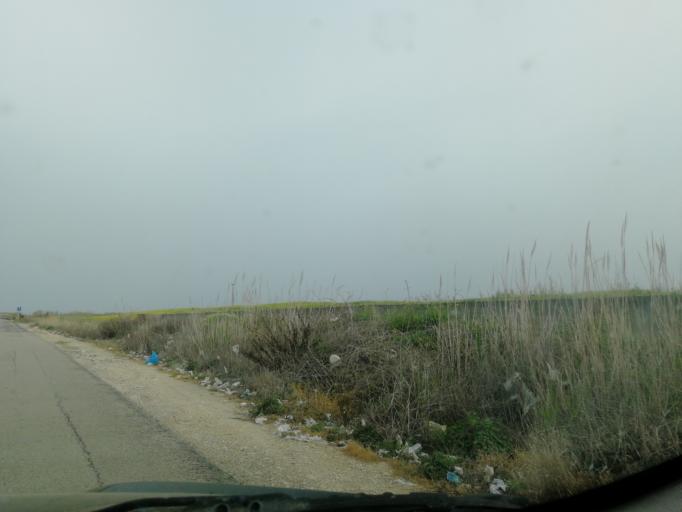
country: IT
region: Apulia
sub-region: Provincia di Barletta - Andria - Trani
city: Barletta
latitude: 41.3175
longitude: 16.3073
